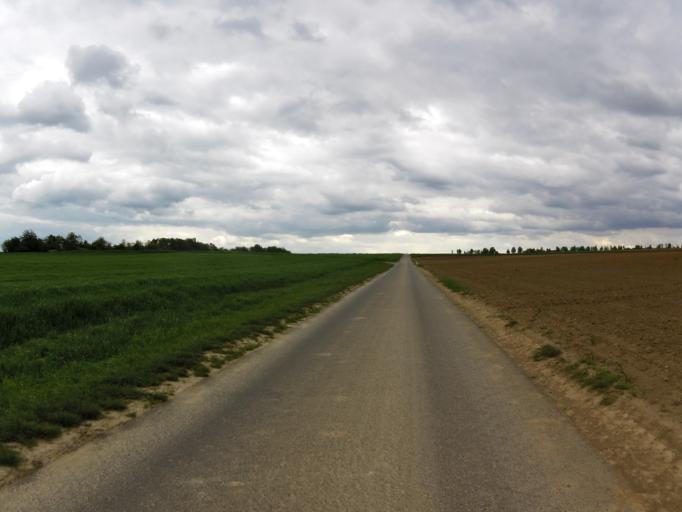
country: DE
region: Bavaria
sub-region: Regierungsbezirk Unterfranken
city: Unterpleichfeld
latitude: 49.8590
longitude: 10.0555
